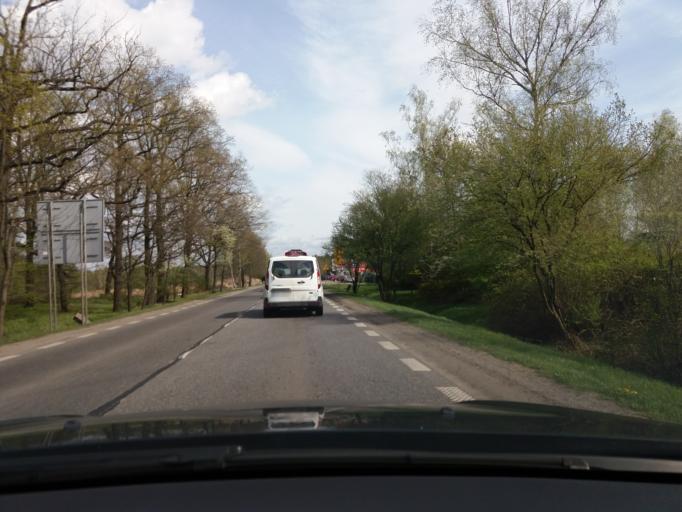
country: PL
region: Lower Silesian Voivodeship
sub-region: Powiat sredzki
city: Mrozow
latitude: 51.1505
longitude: 16.8308
